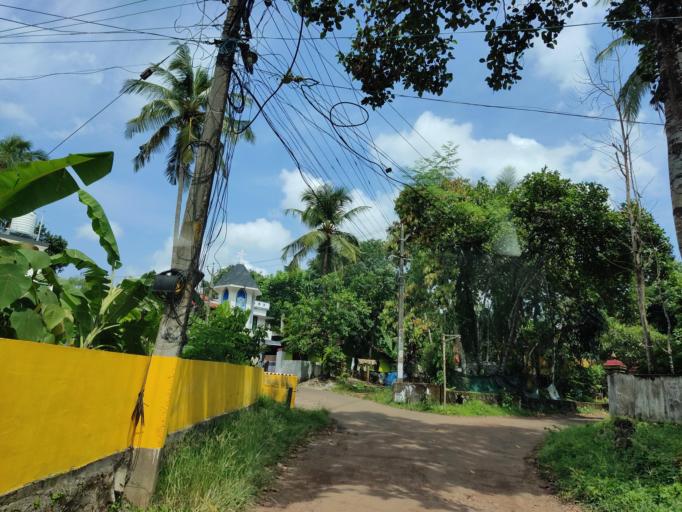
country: IN
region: Kerala
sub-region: Alappuzha
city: Mavelikara
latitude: 9.2599
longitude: 76.5640
